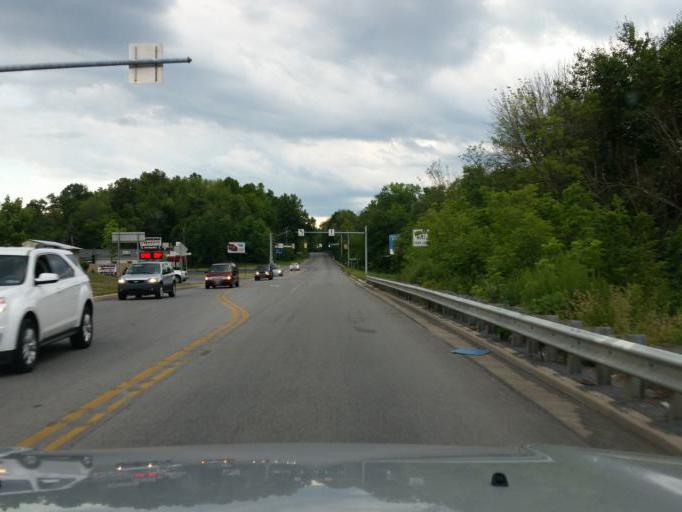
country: US
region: Pennsylvania
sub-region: Blair County
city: Greenwood
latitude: 40.5361
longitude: -78.3743
